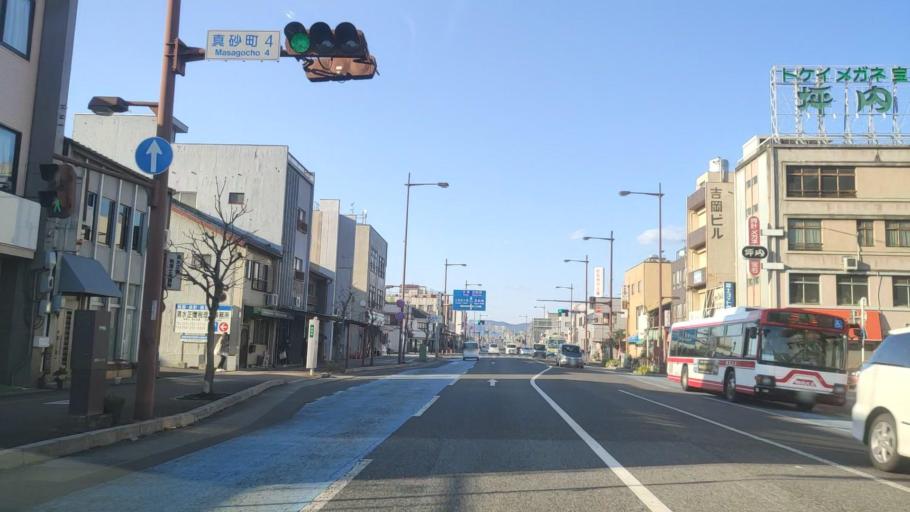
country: JP
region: Gifu
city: Gifu-shi
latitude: 35.4240
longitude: 136.7517
